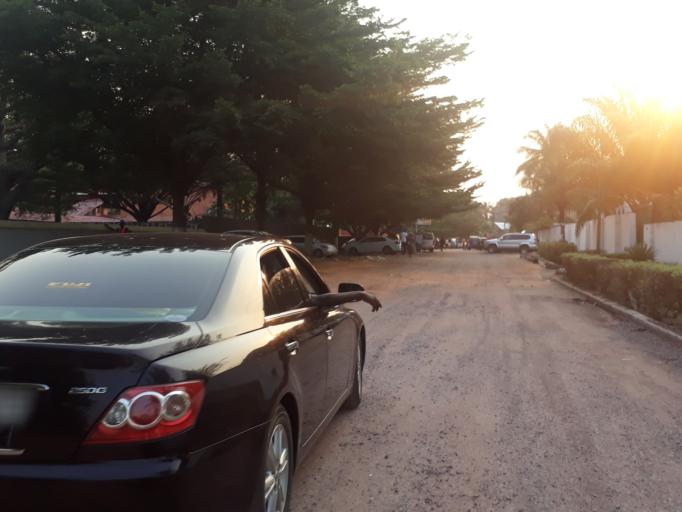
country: CD
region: Kinshasa
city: Kinshasa
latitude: -4.3093
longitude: 15.2999
